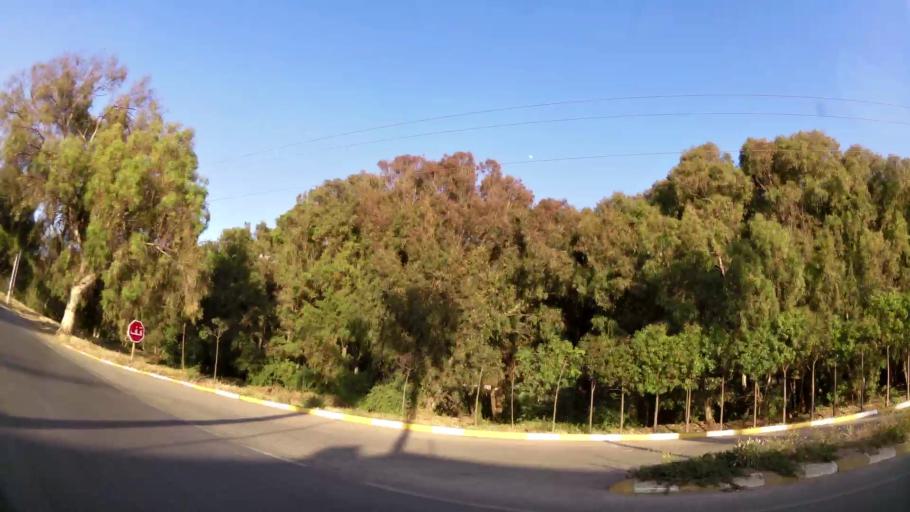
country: MA
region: Rabat-Sale-Zemmour-Zaer
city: Sale
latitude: 34.1088
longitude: -6.7523
